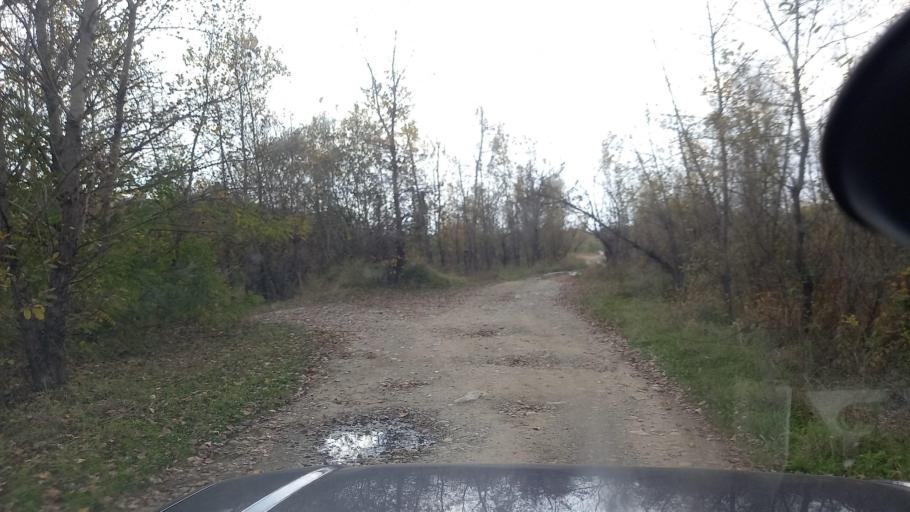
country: RU
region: Krasnodarskiy
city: Shedok
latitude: 44.1762
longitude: 40.8505
